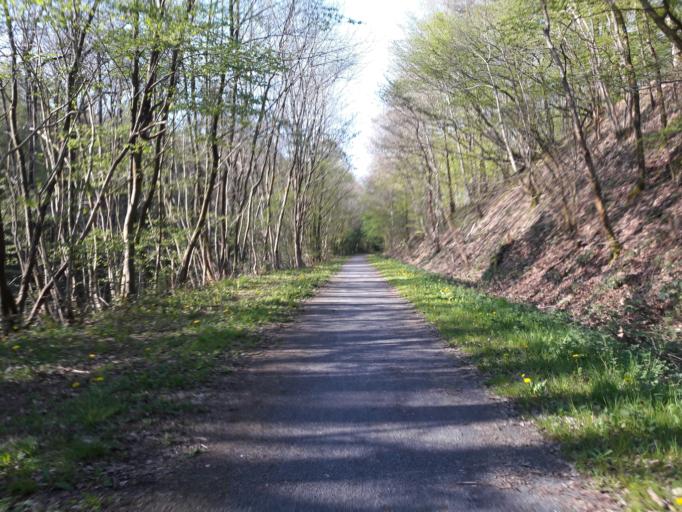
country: FR
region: Nord-Pas-de-Calais
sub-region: Departement du Nord
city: Sains-du-Nord
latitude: 50.1358
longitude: 4.0662
